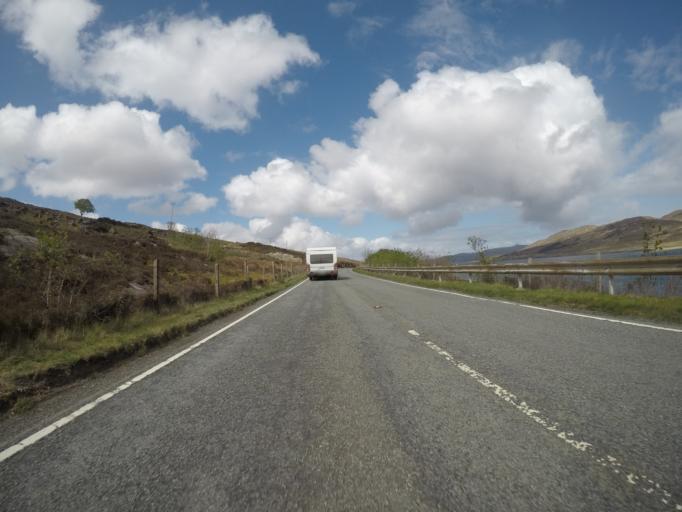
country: GB
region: Scotland
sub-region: Highland
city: Portree
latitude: 57.2812
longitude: -6.0119
